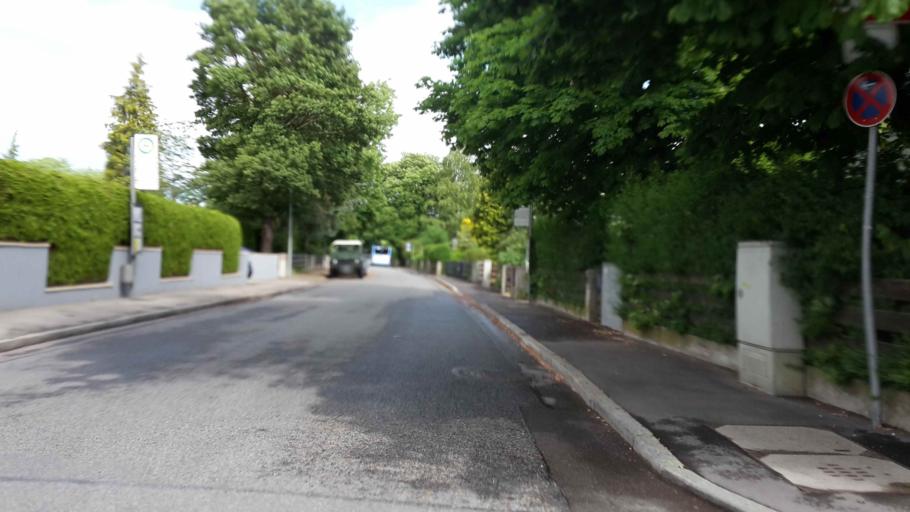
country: DE
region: Bavaria
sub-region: Upper Bavaria
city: Karlsfeld
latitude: 48.1992
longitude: 11.5185
